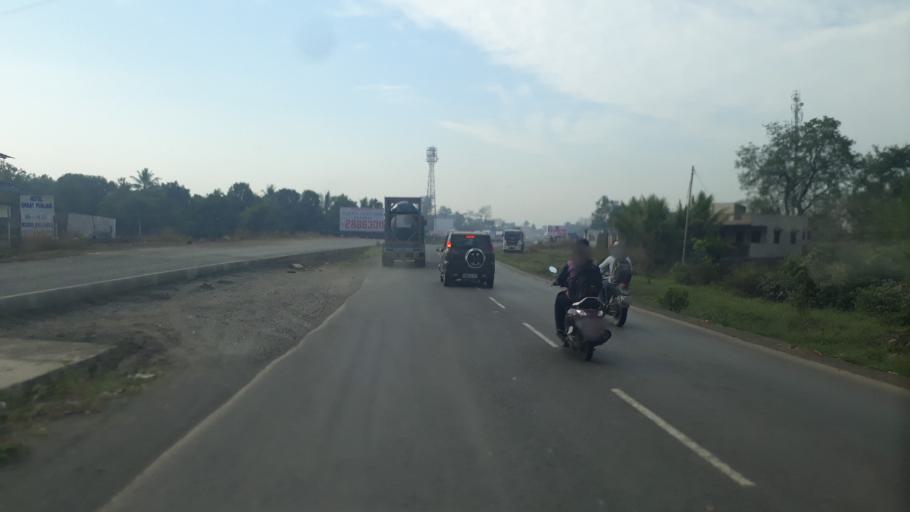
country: IN
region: Maharashtra
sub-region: Raigarh
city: Pen
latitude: 18.8183
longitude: 73.0913
